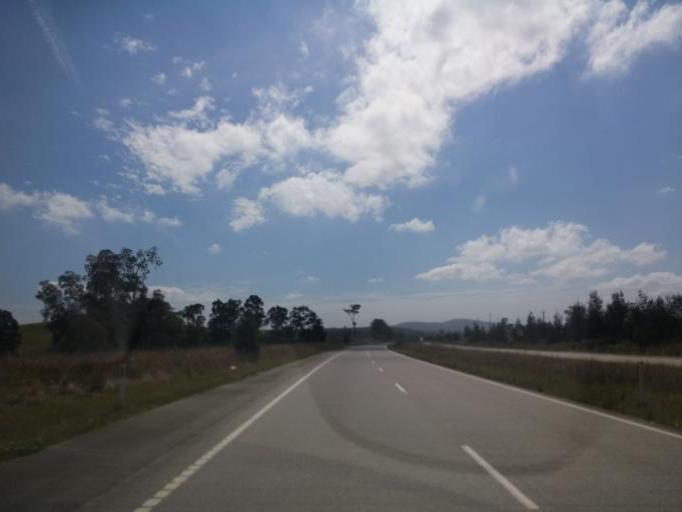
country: AU
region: New South Wales
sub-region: Great Lakes
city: Hawks Nest
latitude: -32.5734
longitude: 152.1304
